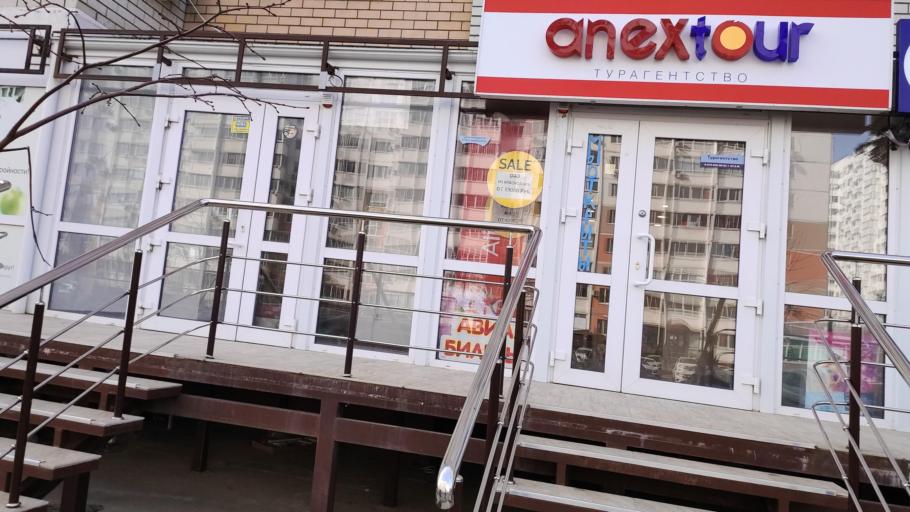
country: RU
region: Krasnodarskiy
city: Krasnodar
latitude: 45.0711
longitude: 39.0069
